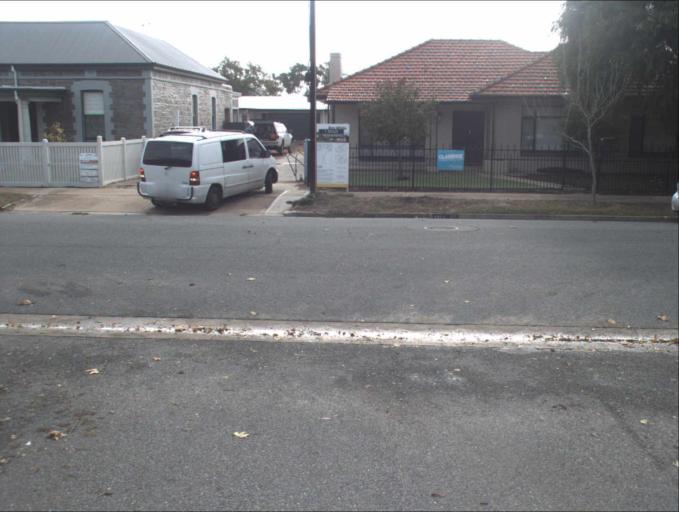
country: AU
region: South Australia
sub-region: Port Adelaide Enfield
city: Birkenhead
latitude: -34.8370
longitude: 138.4860
